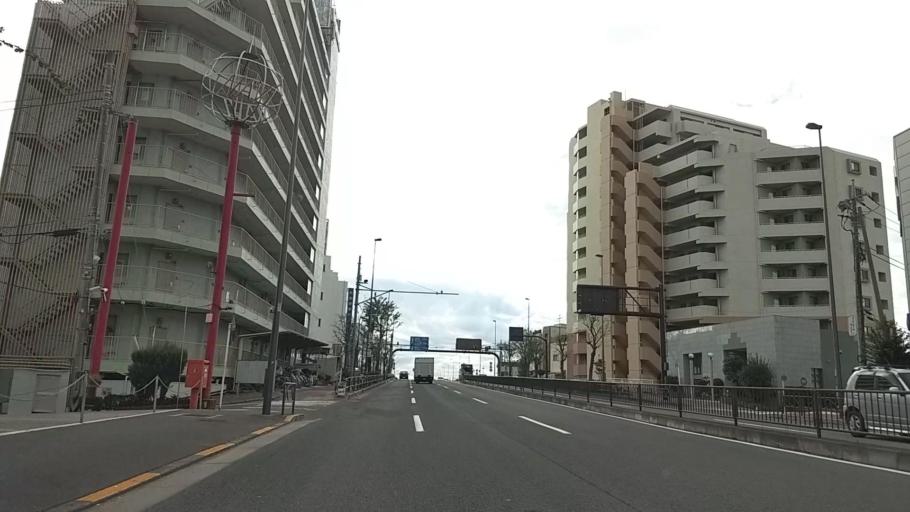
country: JP
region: Kanagawa
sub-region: Kawasaki-shi
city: Kawasaki
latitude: 35.5589
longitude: 139.6971
